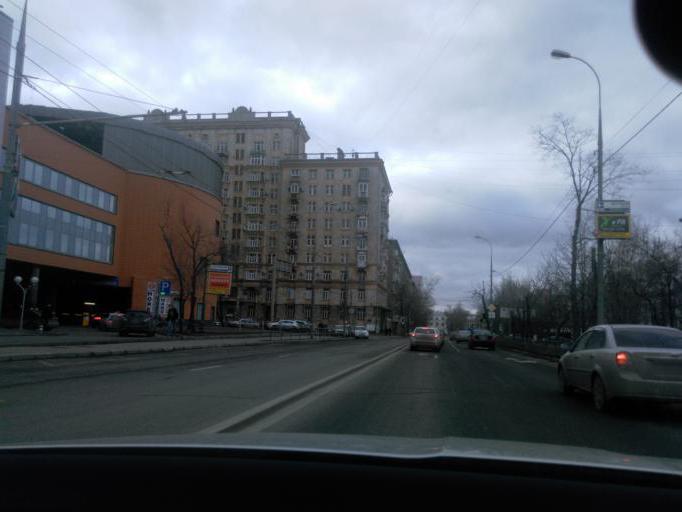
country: RU
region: Moskovskaya
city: Dorogomilovo
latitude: 55.7846
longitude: 37.5589
